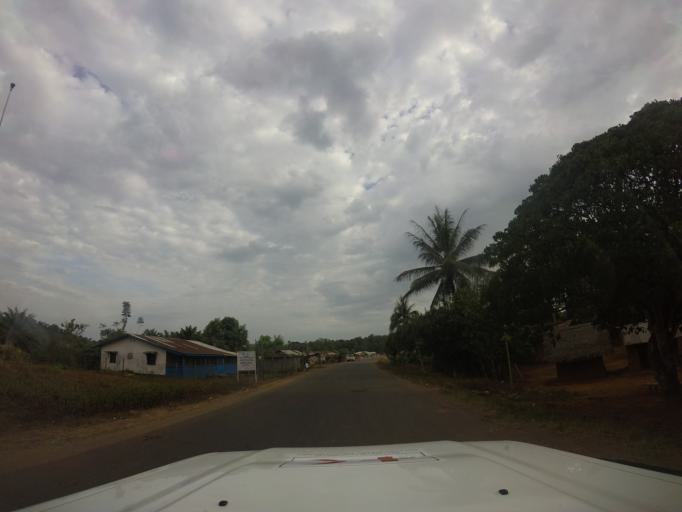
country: LR
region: Grand Cape Mount
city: Robertsport
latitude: 6.7630
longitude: -11.1496
